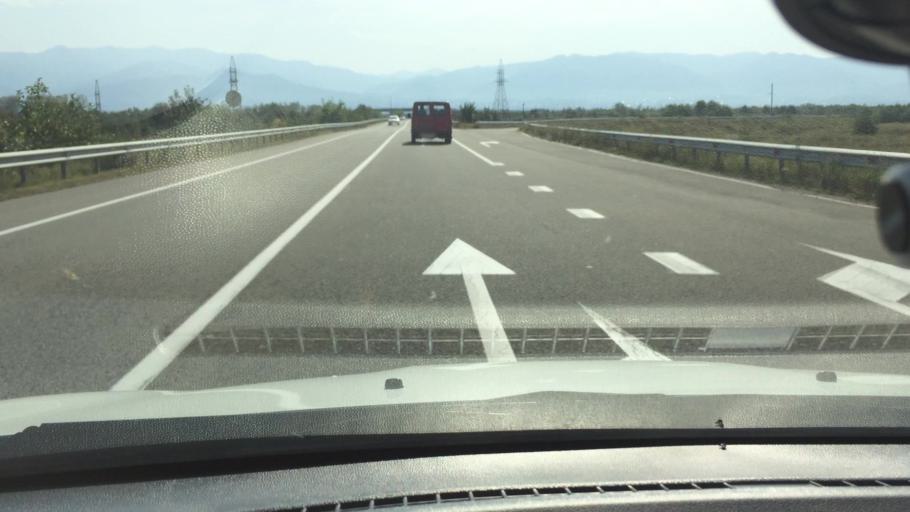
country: GE
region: Ajaria
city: Ochkhamuri
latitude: 41.9030
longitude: 41.7917
